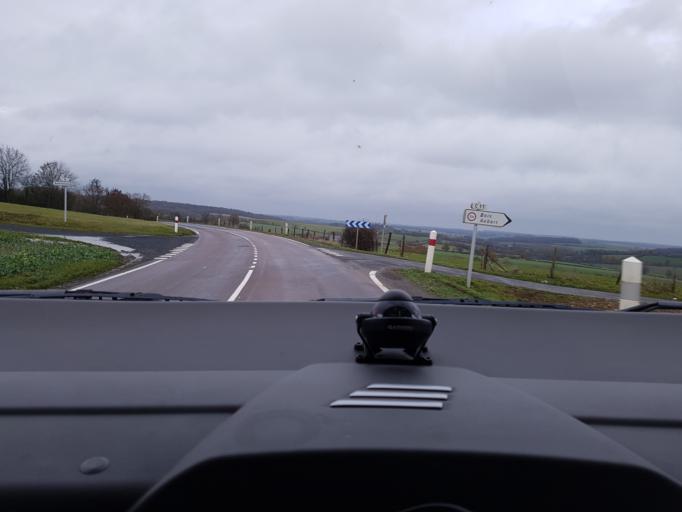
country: FR
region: Picardie
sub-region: Departement de l'Oise
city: Songeons
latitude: 49.5148
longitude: 1.8207
